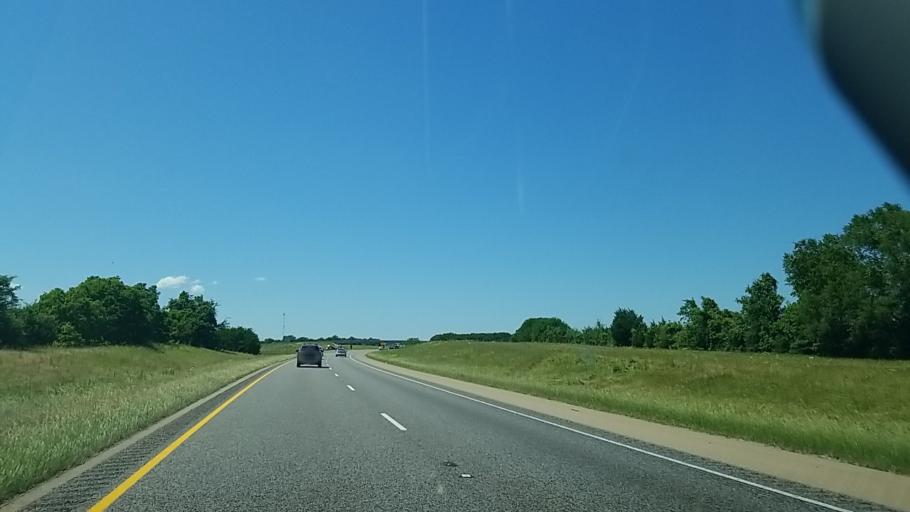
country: US
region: Texas
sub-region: Freestone County
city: Teague
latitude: 31.5808
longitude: -96.1480
